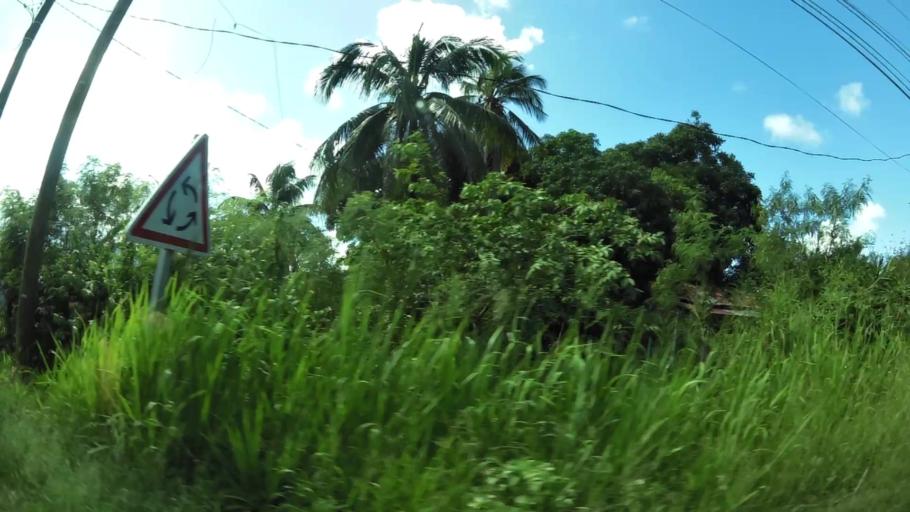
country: GP
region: Guadeloupe
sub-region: Guadeloupe
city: Petit-Canal
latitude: 16.3709
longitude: -61.4519
